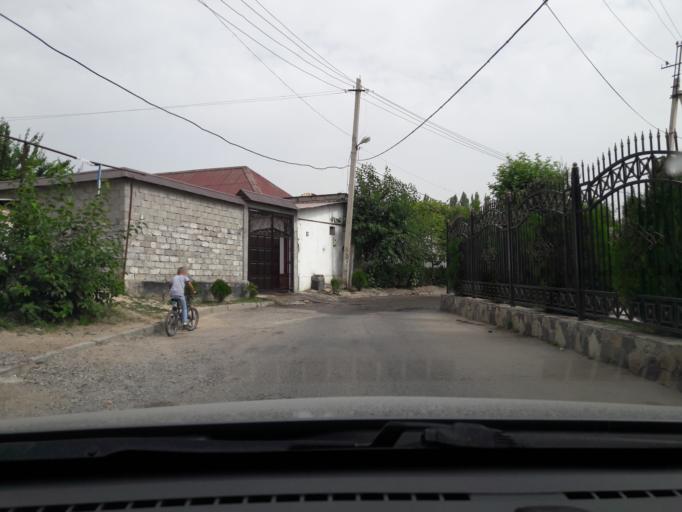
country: TJ
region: Dushanbe
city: Dushanbe
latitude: 38.5801
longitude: 68.7644
